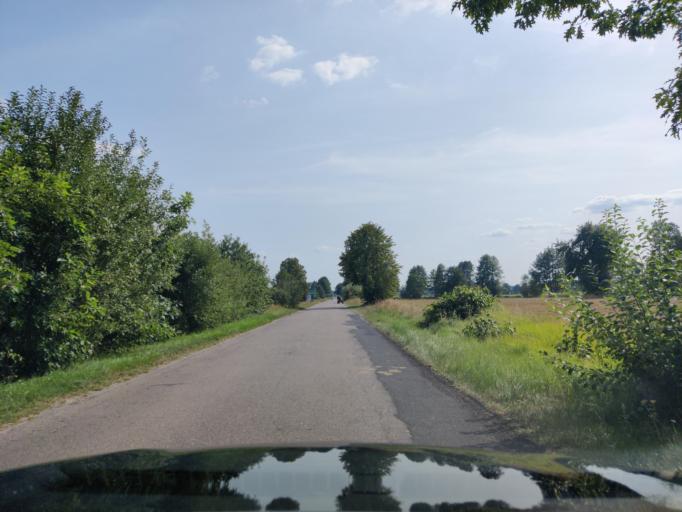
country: PL
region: Masovian Voivodeship
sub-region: Powiat wyszkowski
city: Rzasnik
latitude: 52.7539
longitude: 21.3535
